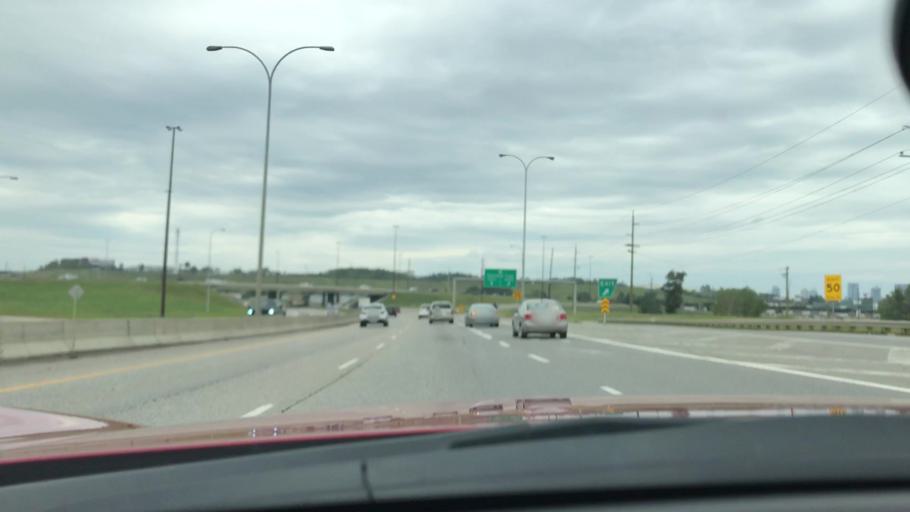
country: CA
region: Alberta
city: Calgary
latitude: 50.9914
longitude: -114.0308
